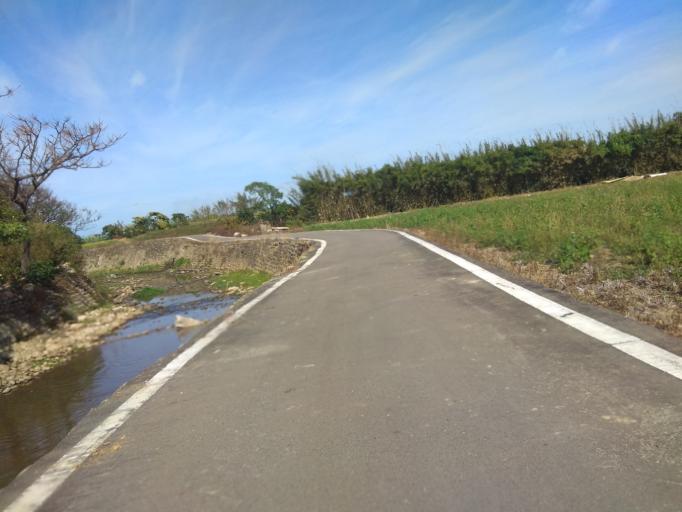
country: TW
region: Taiwan
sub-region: Hsinchu
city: Zhubei
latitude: 25.0205
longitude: 121.0663
